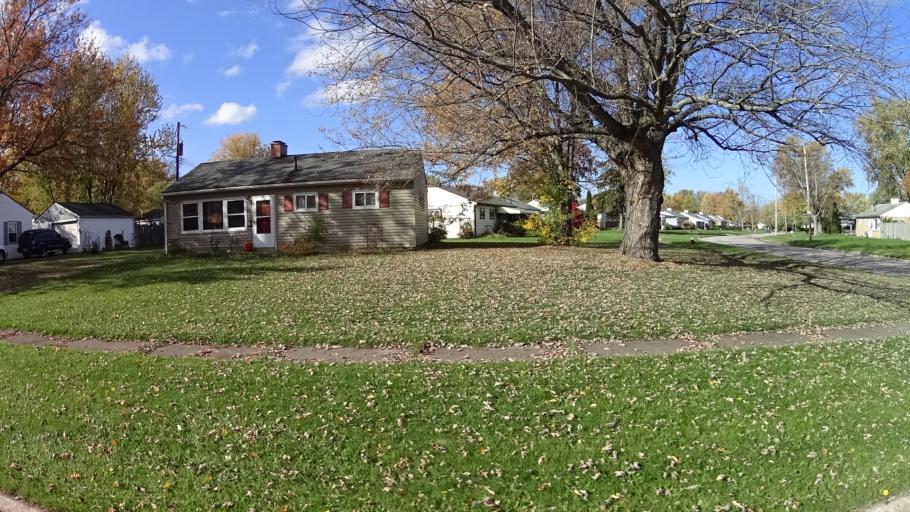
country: US
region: Ohio
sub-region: Lorain County
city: Sheffield
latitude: 41.4316
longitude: -82.1045
